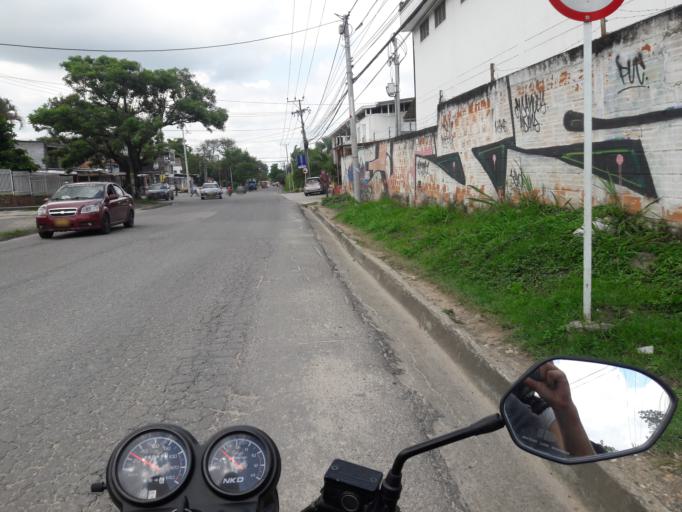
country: CO
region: Tolima
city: Ibague
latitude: 4.4470
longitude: -75.1604
